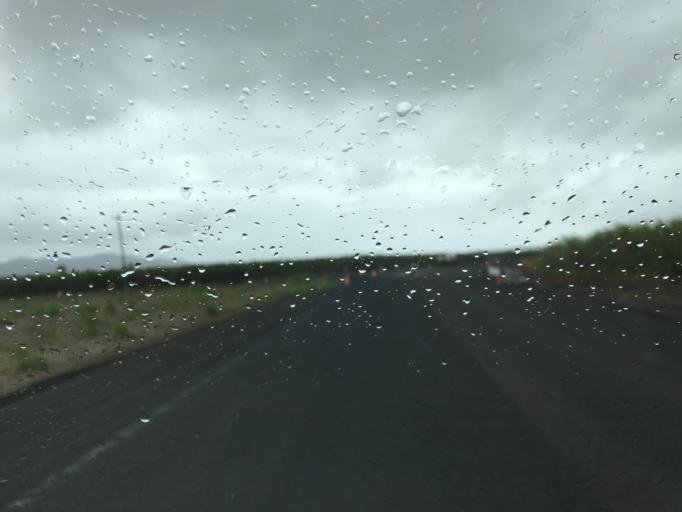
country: AU
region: Queensland
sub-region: Cassowary Coast
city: Innisfail
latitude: -17.5001
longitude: 145.9867
